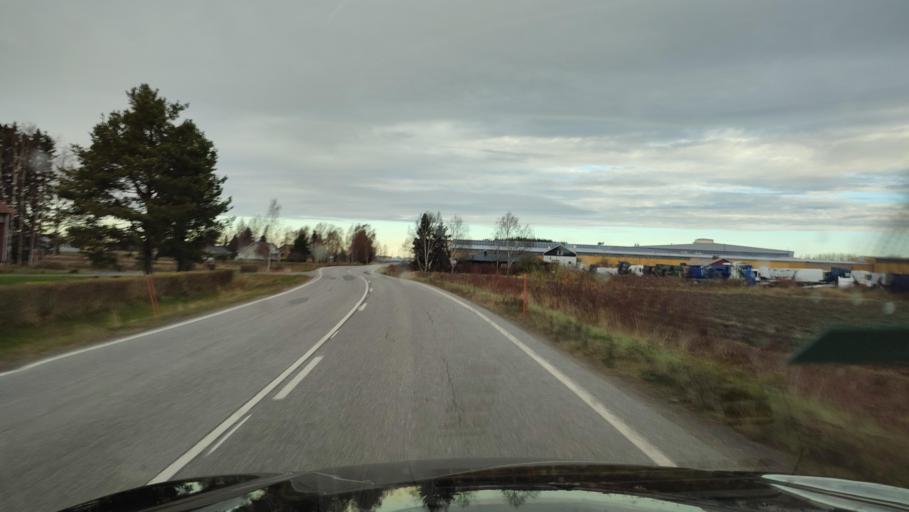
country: FI
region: Ostrobothnia
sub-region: Sydosterbotten
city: Naerpes
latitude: 62.4390
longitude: 21.3520
